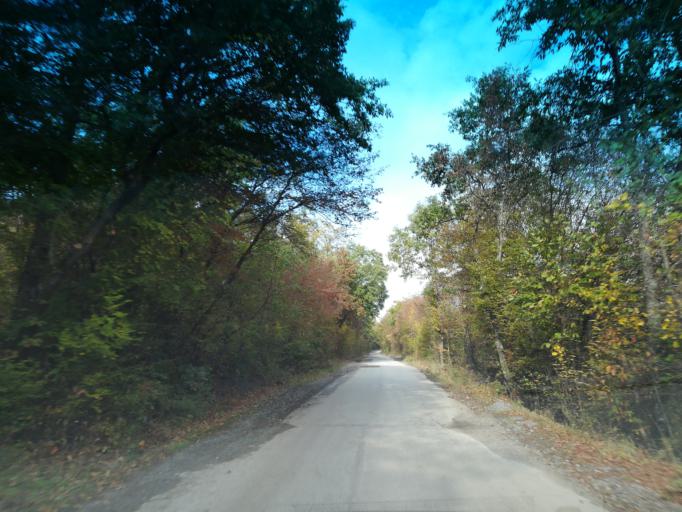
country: BG
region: Stara Zagora
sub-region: Obshtina Nikolaevo
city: Elkhovo
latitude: 42.3184
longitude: 25.4049
